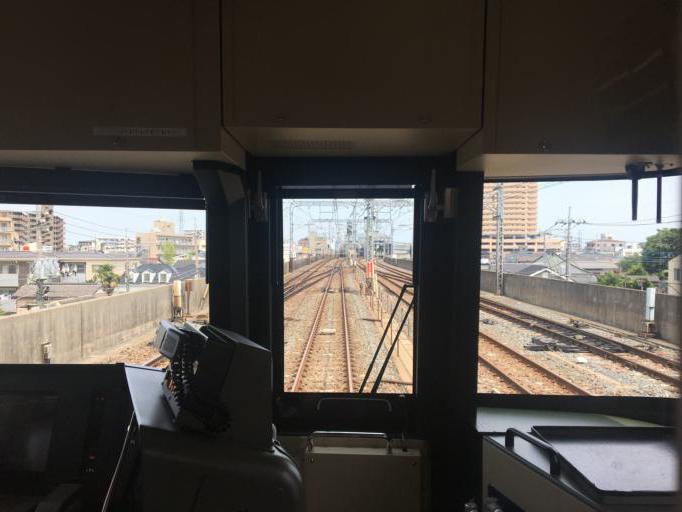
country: JP
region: Saitama
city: Koshigaya
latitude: 35.8986
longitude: 139.7810
